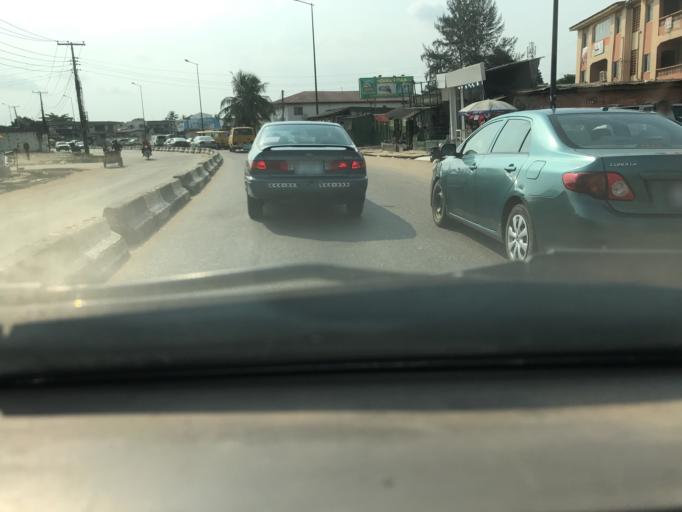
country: NG
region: Lagos
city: Agege
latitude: 6.6021
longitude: 3.3025
